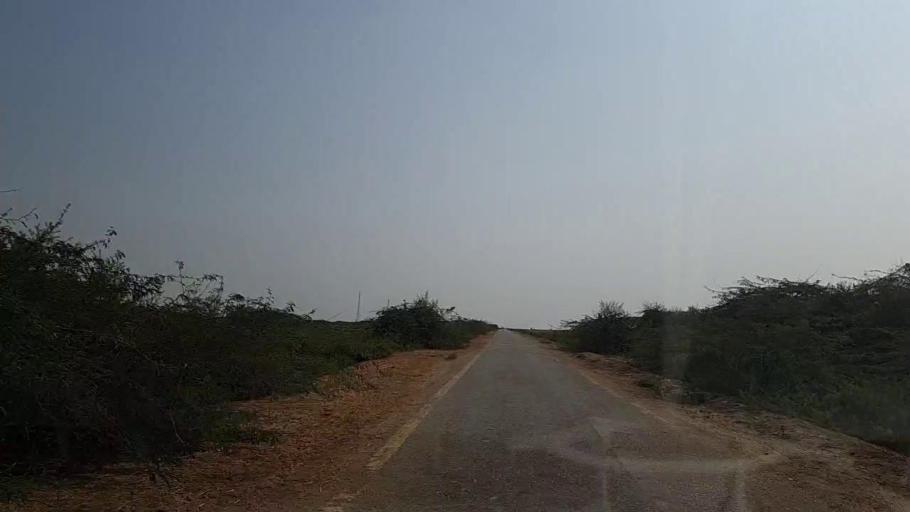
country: PK
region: Sindh
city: Chuhar Jamali
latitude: 24.1734
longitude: 67.8919
